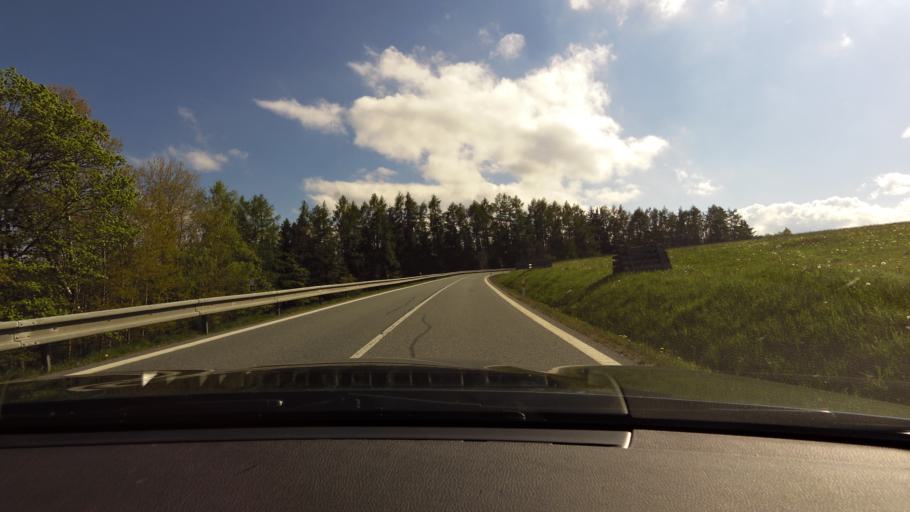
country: CZ
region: Plzensky
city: Strazov
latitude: 49.2492
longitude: 13.3070
